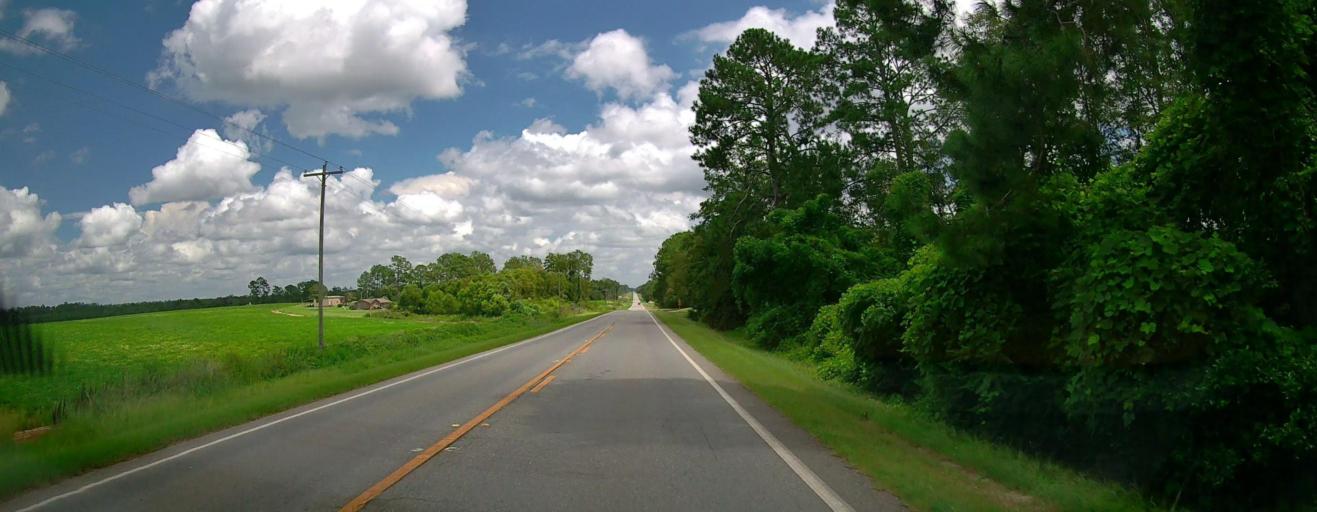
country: US
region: Georgia
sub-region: Turner County
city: Ashburn
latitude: 31.7216
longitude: -83.5133
